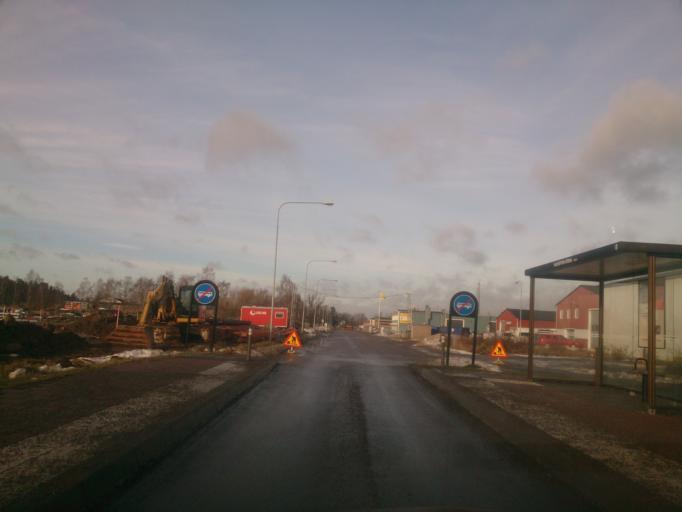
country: SE
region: OEstergoetland
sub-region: Linkopings Kommun
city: Sturefors
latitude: 58.3926
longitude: 15.7036
